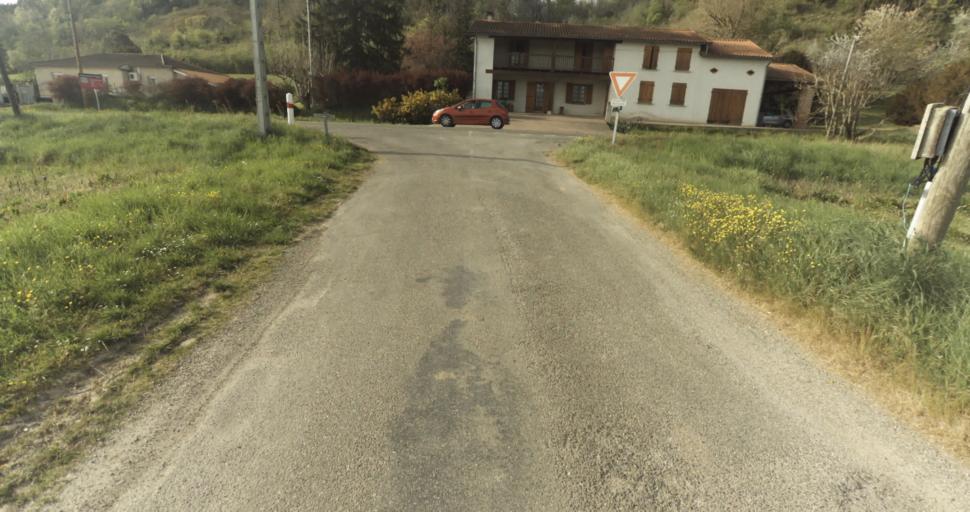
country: FR
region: Midi-Pyrenees
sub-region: Departement du Tarn-et-Garonne
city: Moissac
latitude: 44.1209
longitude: 1.1265
